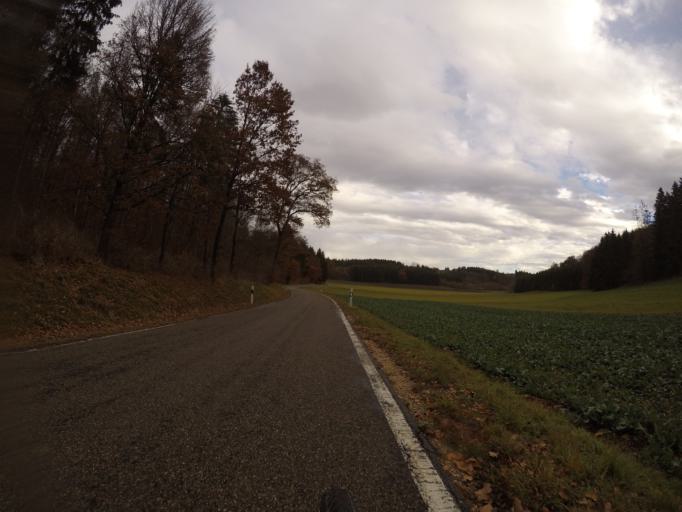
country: DE
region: Baden-Wuerttemberg
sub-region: Tuebingen Region
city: Sankt Johann
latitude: 48.4090
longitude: 9.2990
